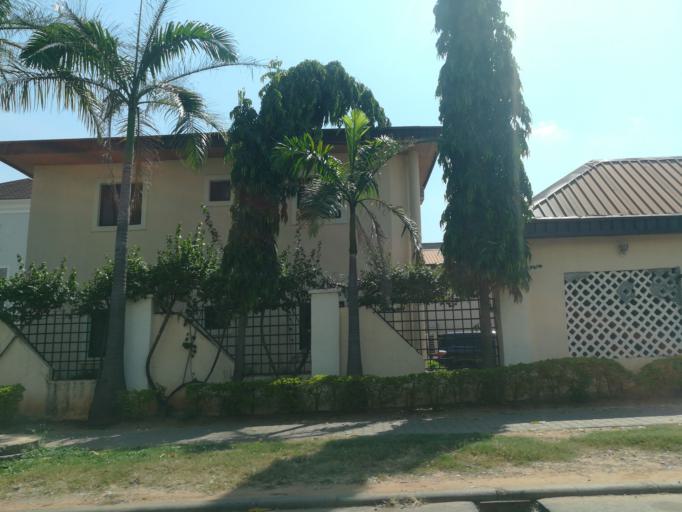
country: NG
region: Abuja Federal Capital Territory
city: Abuja
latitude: 9.0731
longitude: 7.4316
